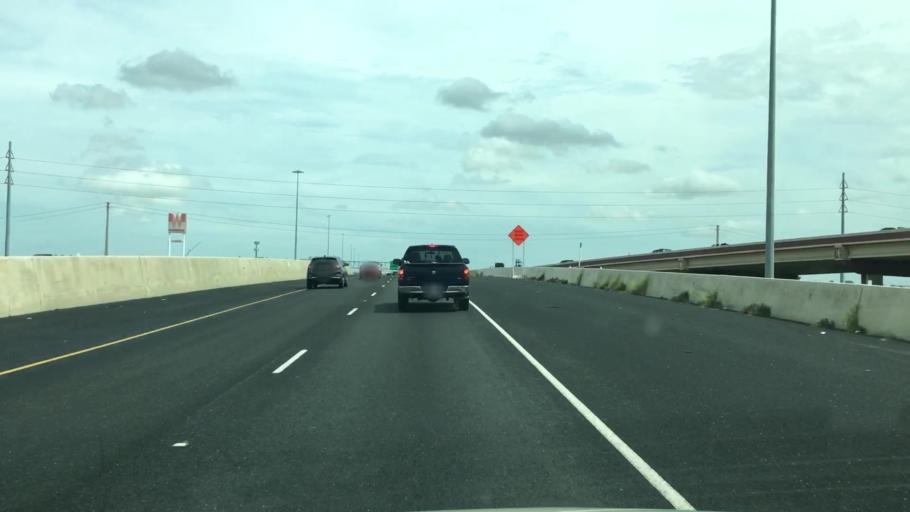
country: US
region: Texas
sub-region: Nueces County
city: Corpus Christi
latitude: 27.7363
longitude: -97.4290
